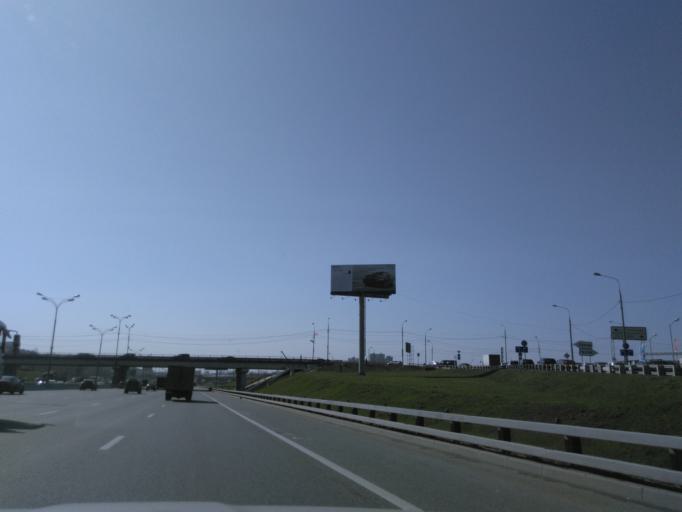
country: RU
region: Moskovskaya
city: Nemchinovka
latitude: 55.7248
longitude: 37.3798
